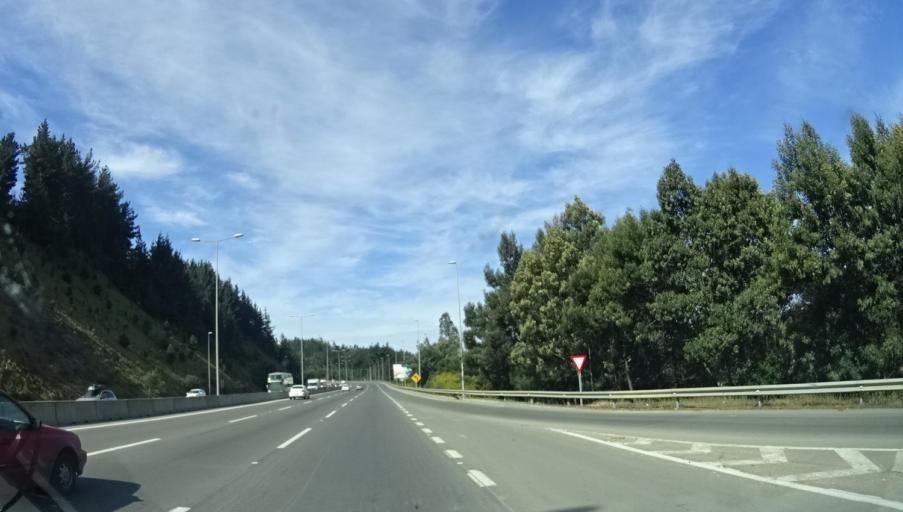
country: CL
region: Valparaiso
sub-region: Provincia de Valparaiso
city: Vina del Mar
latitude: -33.1081
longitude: -71.5536
